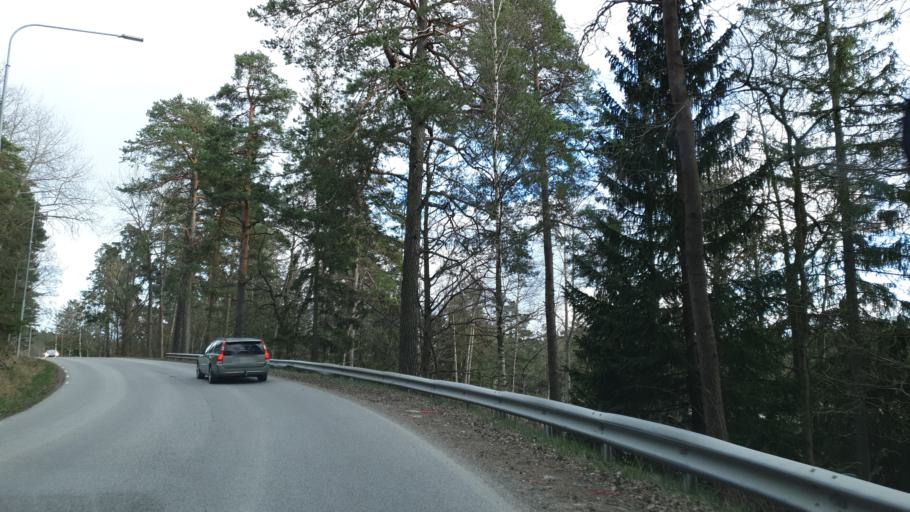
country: SE
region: Stockholm
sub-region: Lidingo
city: Lidingoe
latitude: 59.3804
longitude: 18.1233
